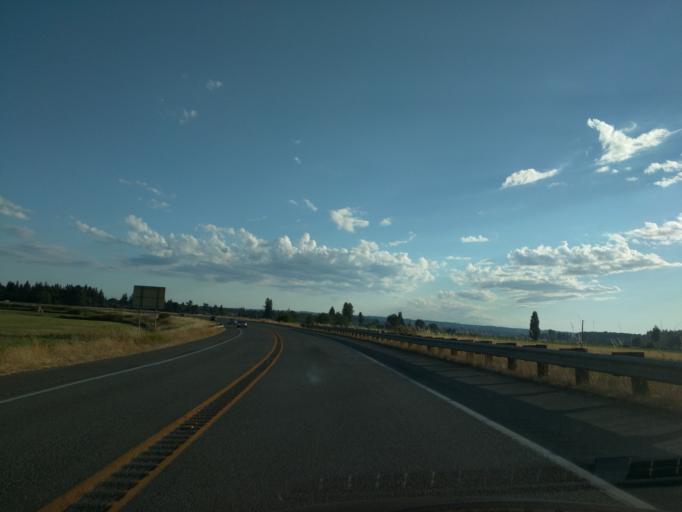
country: US
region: Washington
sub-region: Snohomish County
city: Arlington
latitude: 48.1975
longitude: -122.1366
